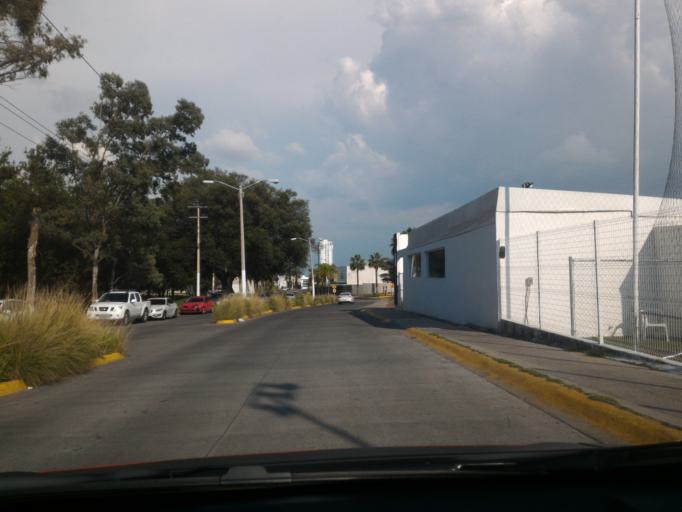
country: MX
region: Jalisco
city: Guadalajara
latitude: 20.6639
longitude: -103.4404
